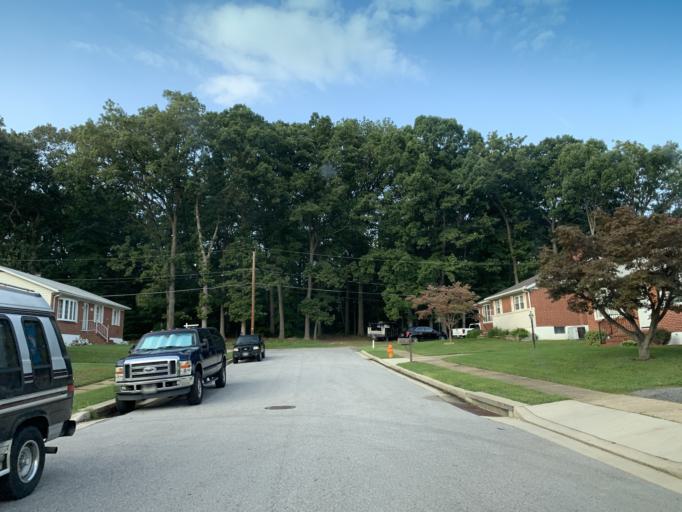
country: US
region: Maryland
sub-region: Baltimore County
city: Essex
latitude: 39.3208
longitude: -76.4665
